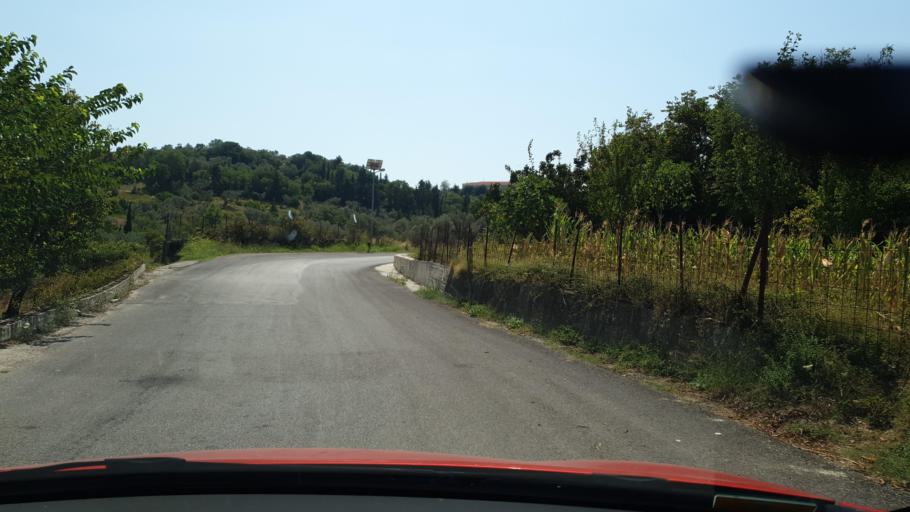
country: GR
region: Central Greece
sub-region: Nomos Evvoias
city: Oxilithos
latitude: 38.5722
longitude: 24.0631
